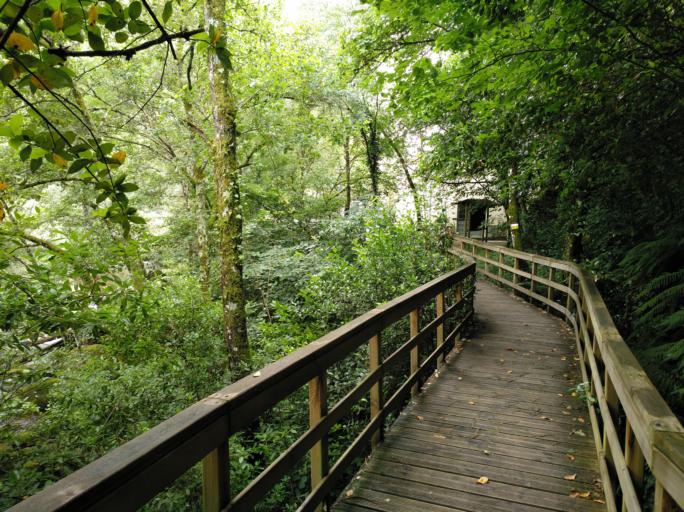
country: ES
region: Galicia
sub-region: Provincia de Lugo
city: Lobios
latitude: 42.3751
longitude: -7.4971
